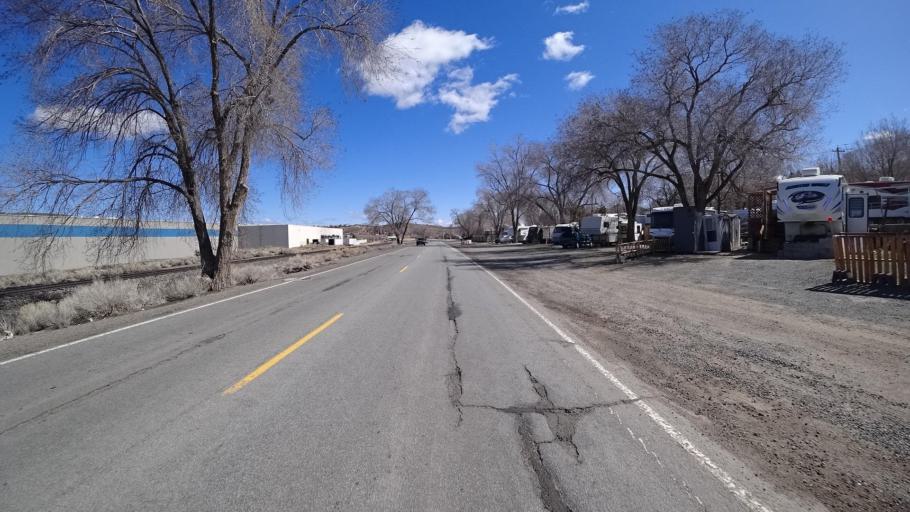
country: US
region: Nevada
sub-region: Washoe County
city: Golden Valley
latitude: 39.5875
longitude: -119.8216
